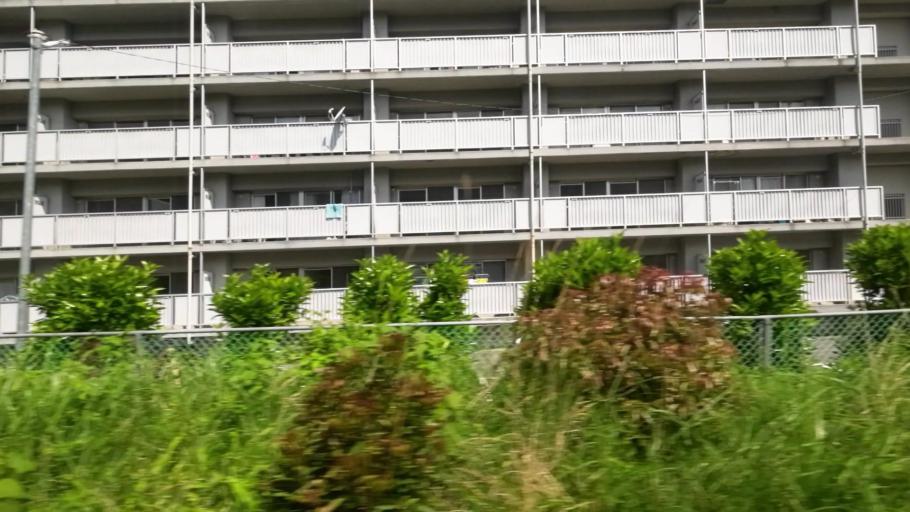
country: JP
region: Ehime
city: Kawanoecho
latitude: 33.9713
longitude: 133.5205
